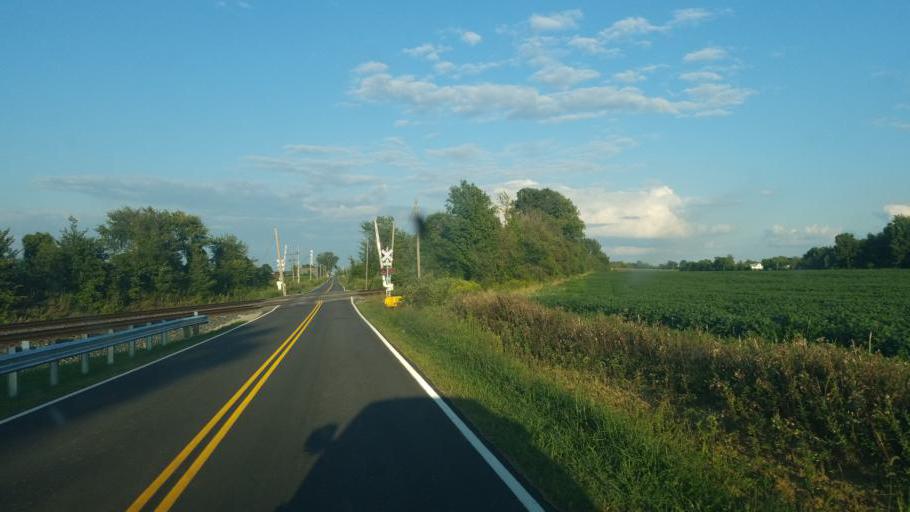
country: US
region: Ohio
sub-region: Huron County
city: Greenwich
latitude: 41.0526
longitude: -82.5949
